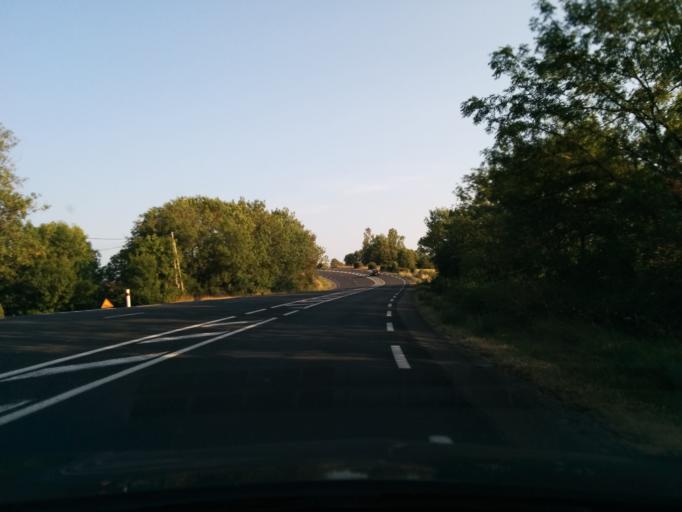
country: FR
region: Midi-Pyrenees
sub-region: Departement du Lot
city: Pradines
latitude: 44.5970
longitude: 1.5153
